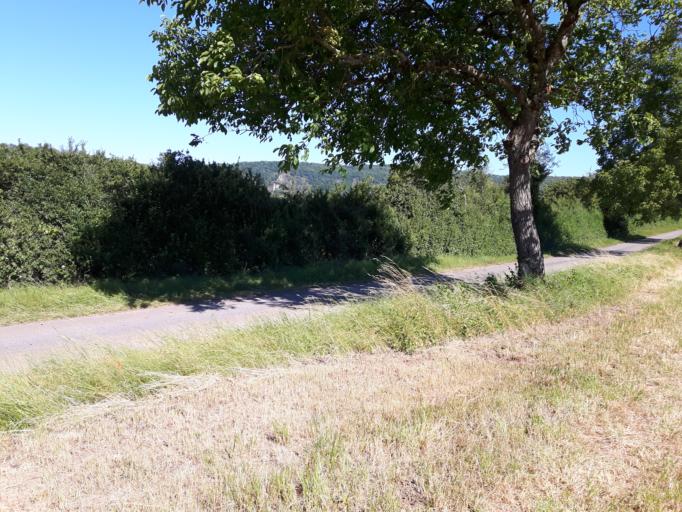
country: FR
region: Franche-Comte
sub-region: Departement du Jura
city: Salins-les-Bains
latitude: 47.0023
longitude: 5.8563
